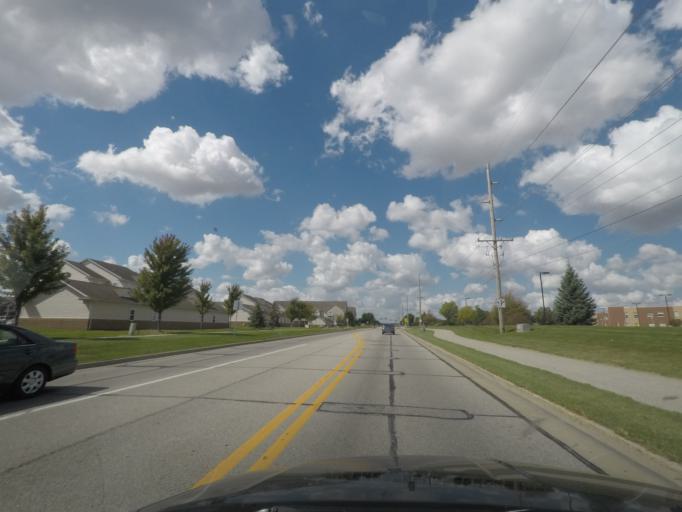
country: US
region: Iowa
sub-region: Story County
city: Ames
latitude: 42.0120
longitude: -93.6699
